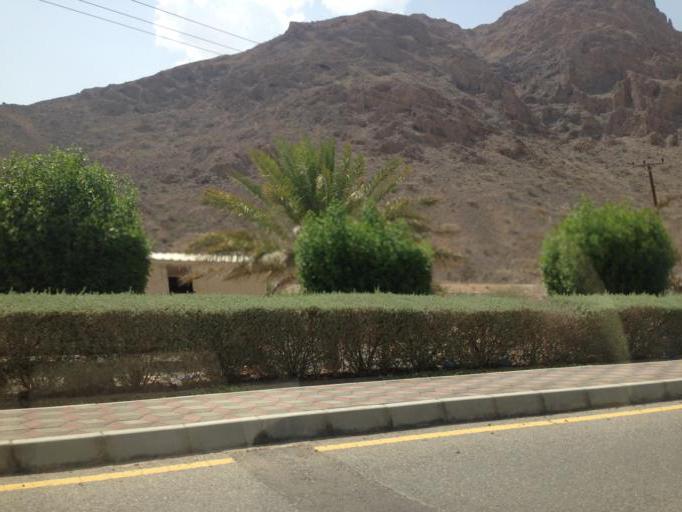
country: OM
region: Ash Sharqiyah
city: Ibra'
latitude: 23.0934
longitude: 58.8505
